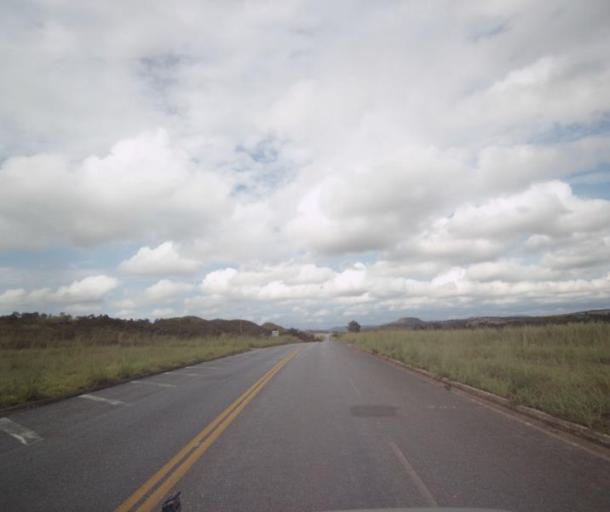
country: BR
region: Goias
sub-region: Pirenopolis
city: Pirenopolis
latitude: -15.5788
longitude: -48.6269
